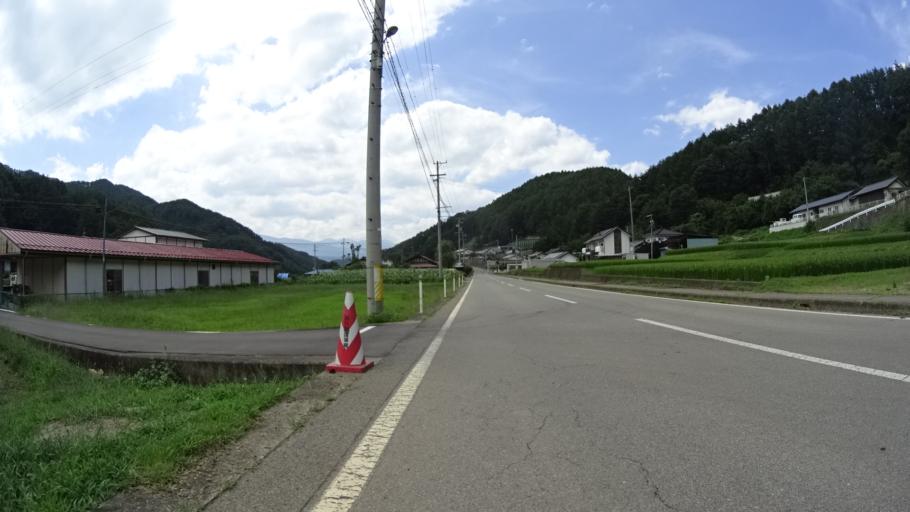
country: JP
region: Nagano
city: Saku
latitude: 36.0598
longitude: 138.5413
